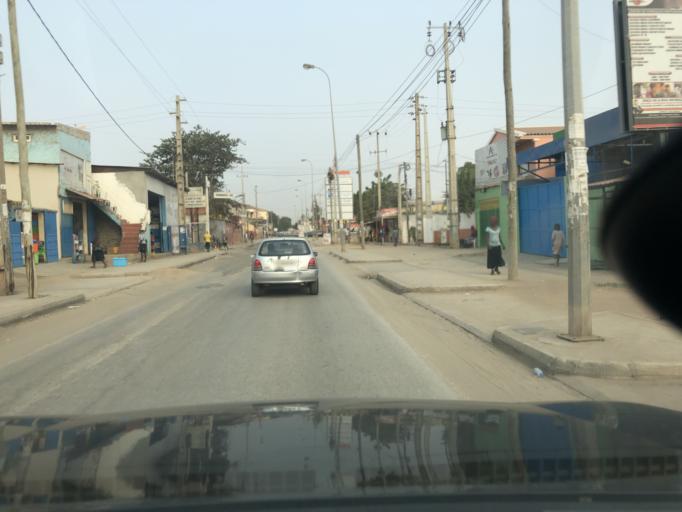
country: AO
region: Luanda
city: Luanda
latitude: -8.8829
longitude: 13.2006
